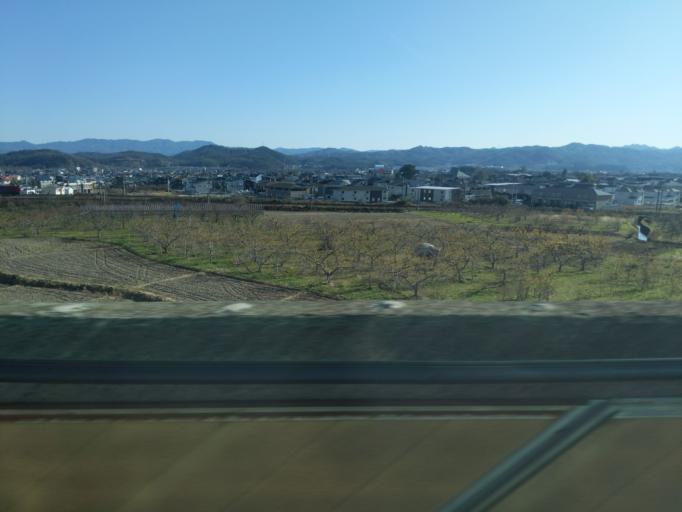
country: JP
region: Fukushima
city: Fukushima-shi
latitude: 37.8095
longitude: 140.4842
